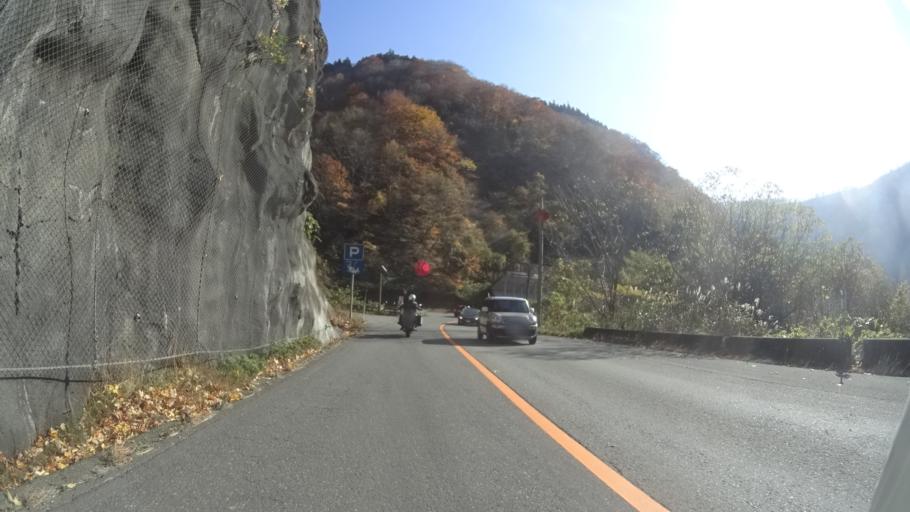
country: JP
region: Fukui
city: Ono
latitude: 35.9335
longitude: 136.6373
